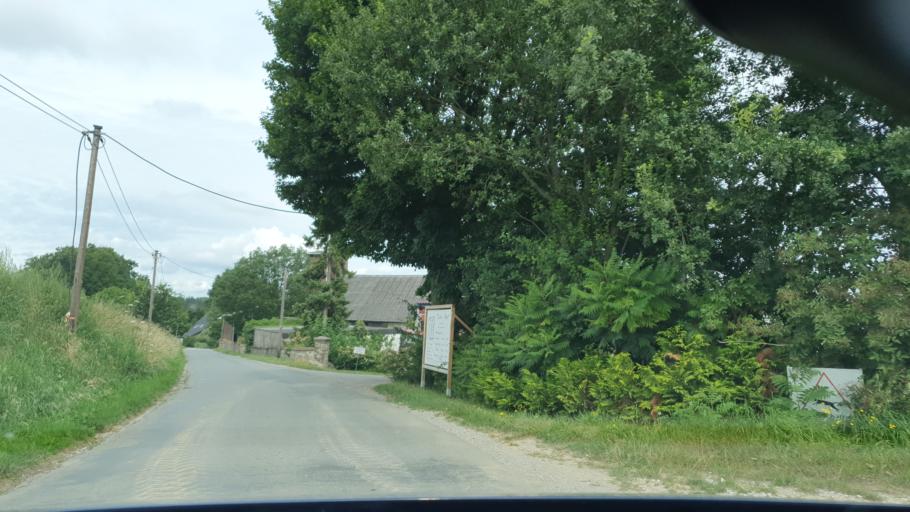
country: DE
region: North Rhine-Westphalia
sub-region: Regierungsbezirk Detmold
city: Werther
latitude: 52.0880
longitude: 8.4129
